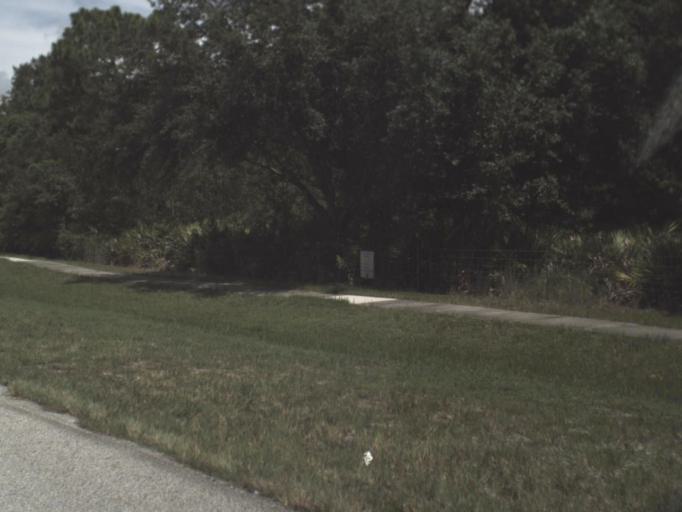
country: US
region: Florida
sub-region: Pasco County
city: Trinity
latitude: 28.1684
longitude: -82.6984
